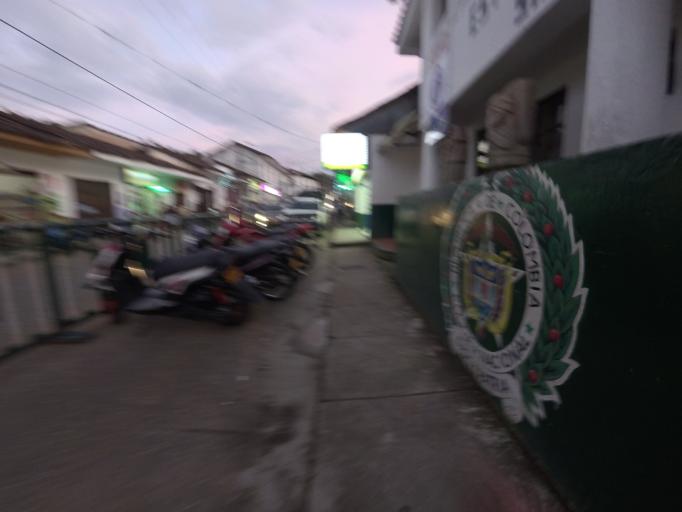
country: CO
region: Huila
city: San Agustin
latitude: 1.8818
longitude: -76.2716
